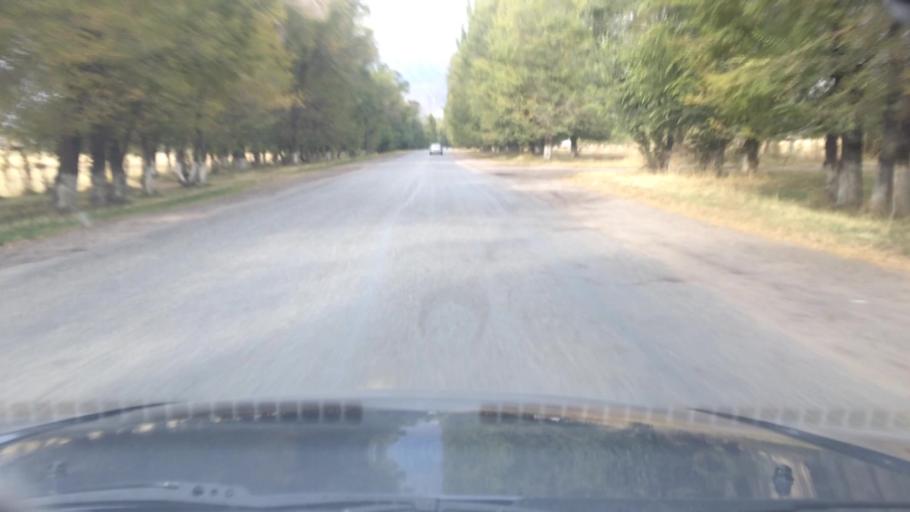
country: KG
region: Ysyk-Koel
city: Tyup
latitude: 42.7852
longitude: 78.2722
